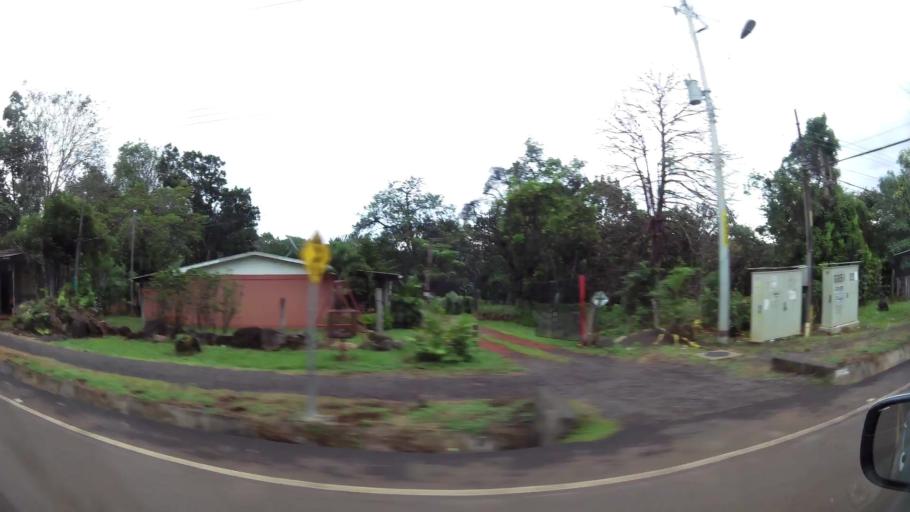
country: CR
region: Alajuela
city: Orotina
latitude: 9.9589
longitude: -84.5897
